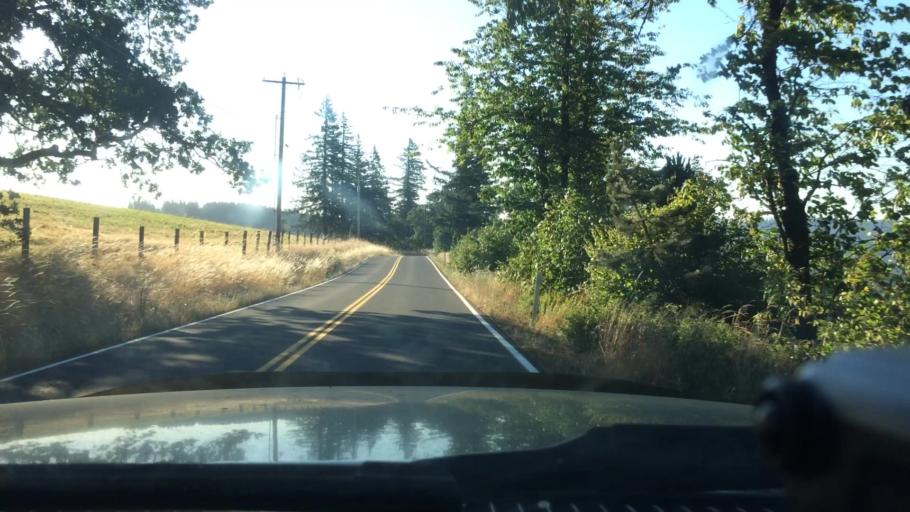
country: US
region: Oregon
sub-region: Yamhill County
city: Newberg
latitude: 45.3375
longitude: -122.9446
